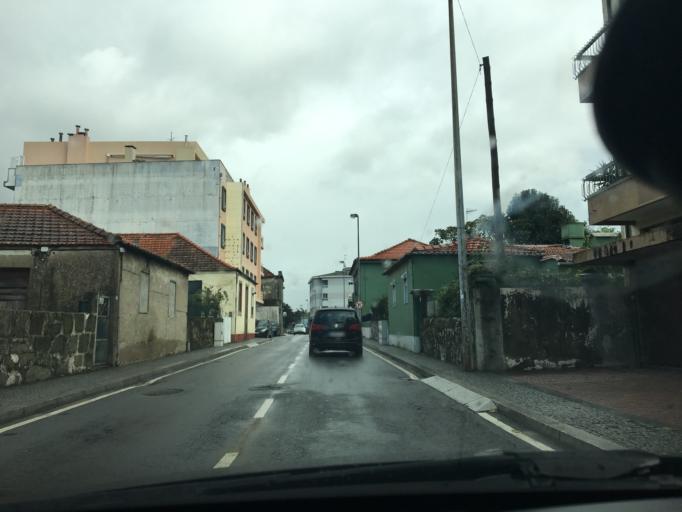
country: PT
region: Porto
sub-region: Matosinhos
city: Santa Cruz do Bispo
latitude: 41.2444
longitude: -8.6652
